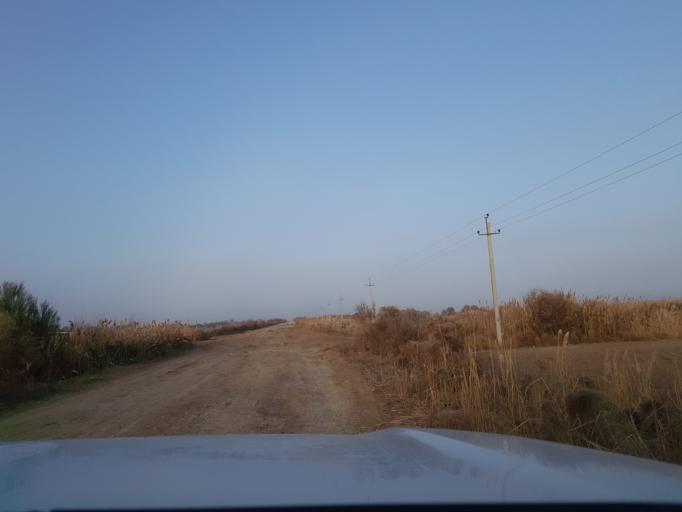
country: TM
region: Dasoguz
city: Koeneuergench
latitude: 41.8462
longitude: 58.3851
